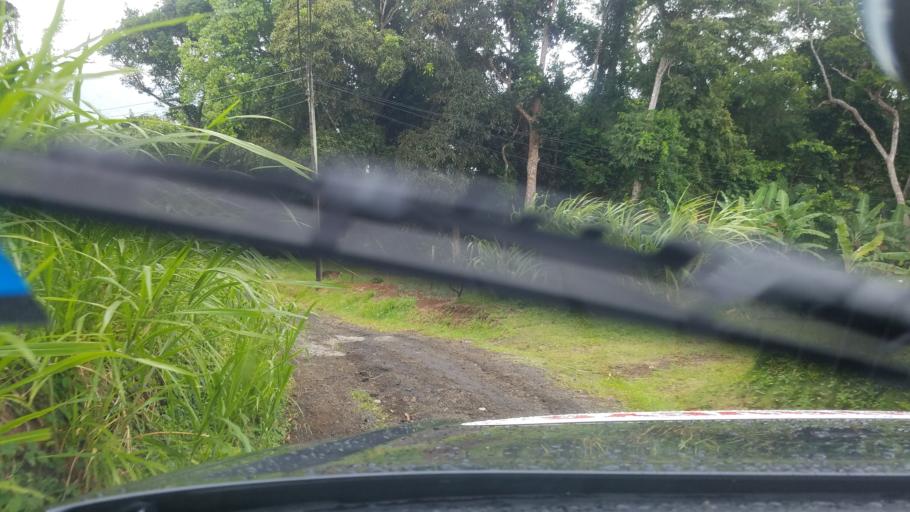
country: LC
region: Castries Quarter
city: Bisee
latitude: 14.0219
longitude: -60.9330
